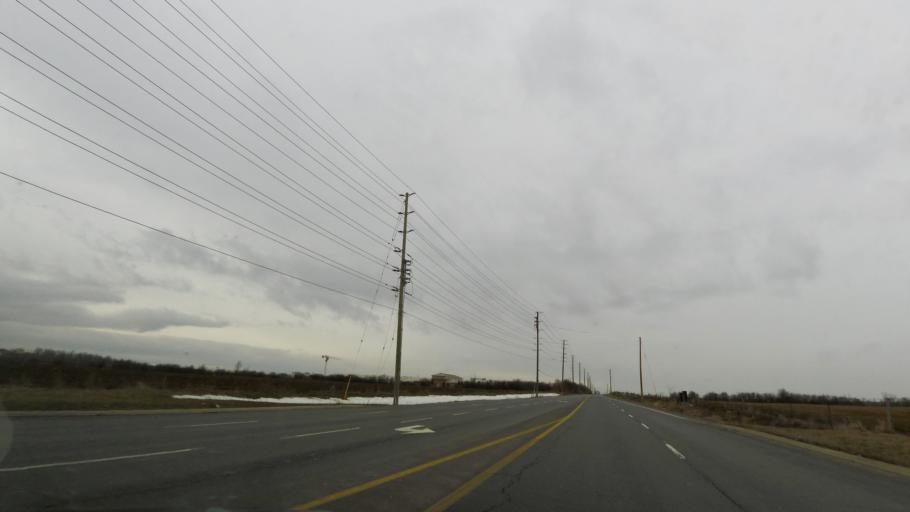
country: CA
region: Ontario
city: Brampton
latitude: 43.7869
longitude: -79.6511
